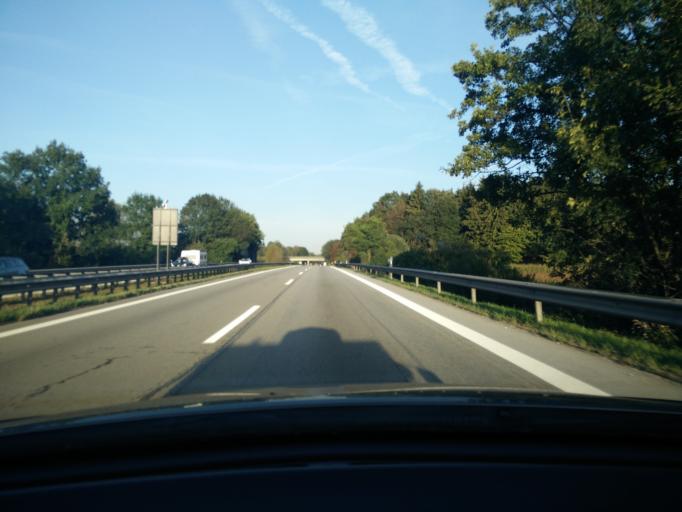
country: DE
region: Bavaria
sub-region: Upper Bavaria
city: Rohrdorf
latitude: 47.8049
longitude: 12.1538
